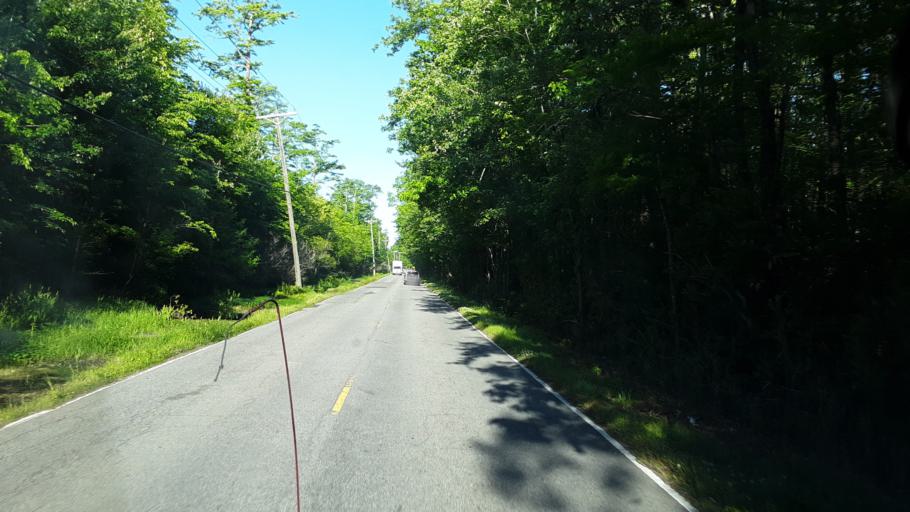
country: US
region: Virginia
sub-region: City of Virginia Beach
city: Virginia Beach
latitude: 36.7222
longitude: -76.0281
